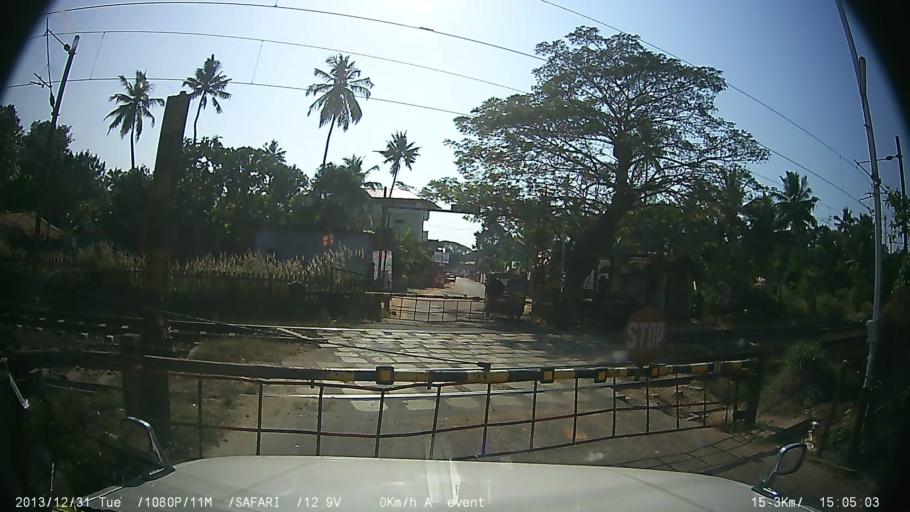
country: IN
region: Kerala
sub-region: Kottayam
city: Vaikam
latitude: 9.7359
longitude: 76.5092
